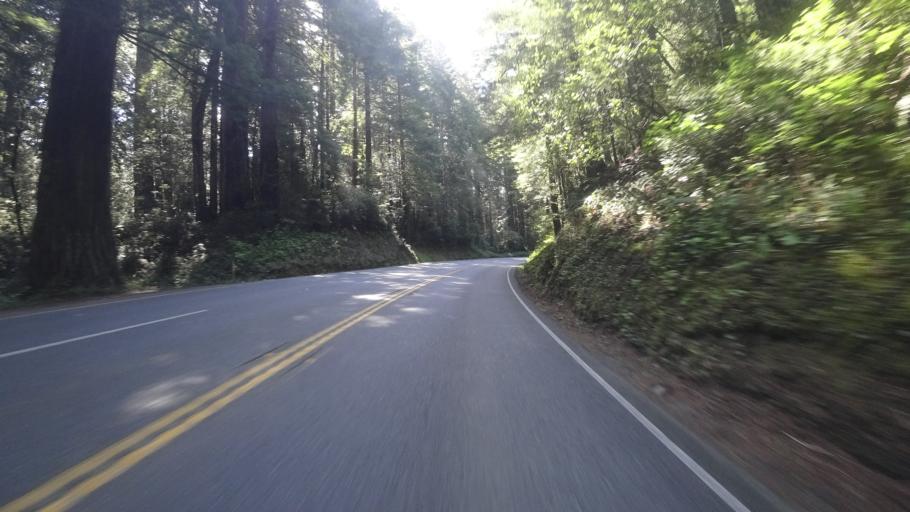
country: US
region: California
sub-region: Del Norte County
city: Bertsch-Oceanview
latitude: 41.6474
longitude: -124.1127
